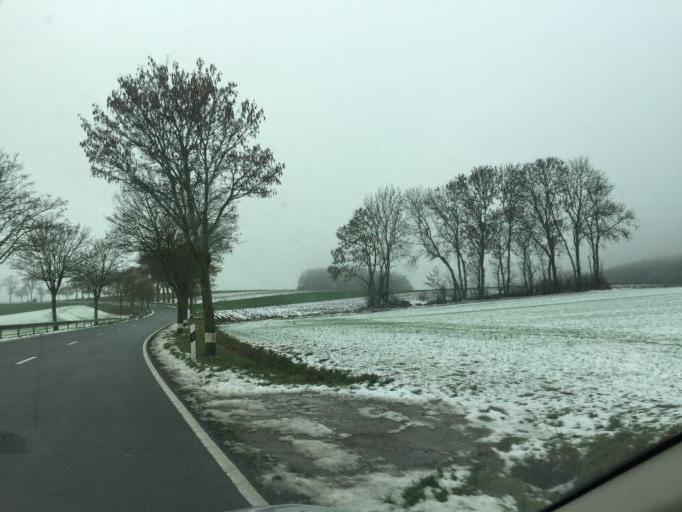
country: LU
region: Diekirch
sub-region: Canton de Redange
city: Grosbous
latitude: 49.8298
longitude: 5.9834
